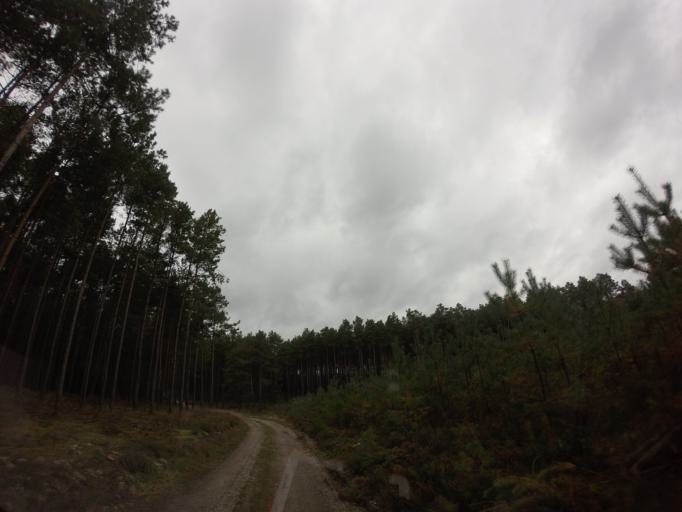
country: PL
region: West Pomeranian Voivodeship
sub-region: Powiat choszczenski
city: Drawno
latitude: 53.1461
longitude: 15.7632
